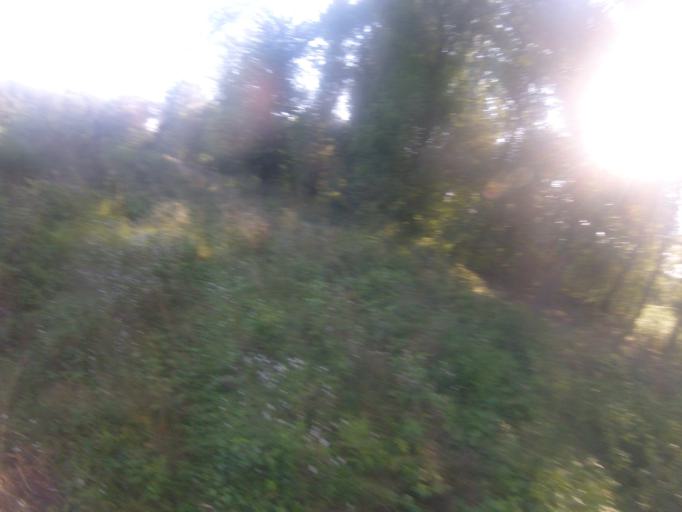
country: HU
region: Bacs-Kiskun
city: Baja
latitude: 46.1829
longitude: 18.9205
